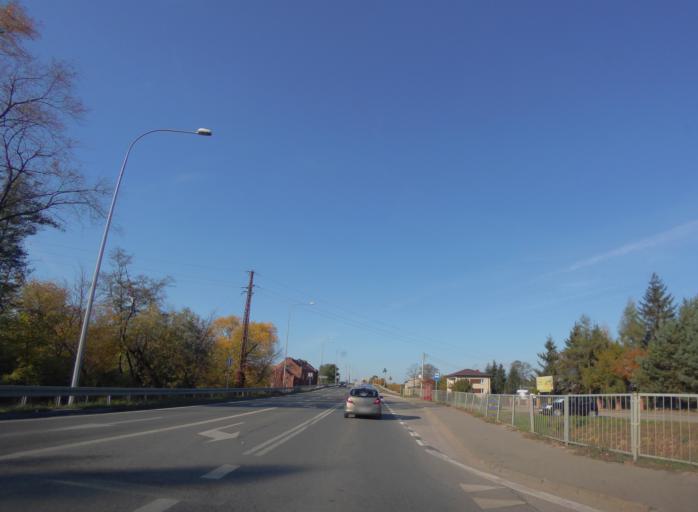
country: PL
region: Masovian Voivodeship
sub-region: Powiat minski
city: Debe Wielkie
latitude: 52.2000
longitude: 21.4241
